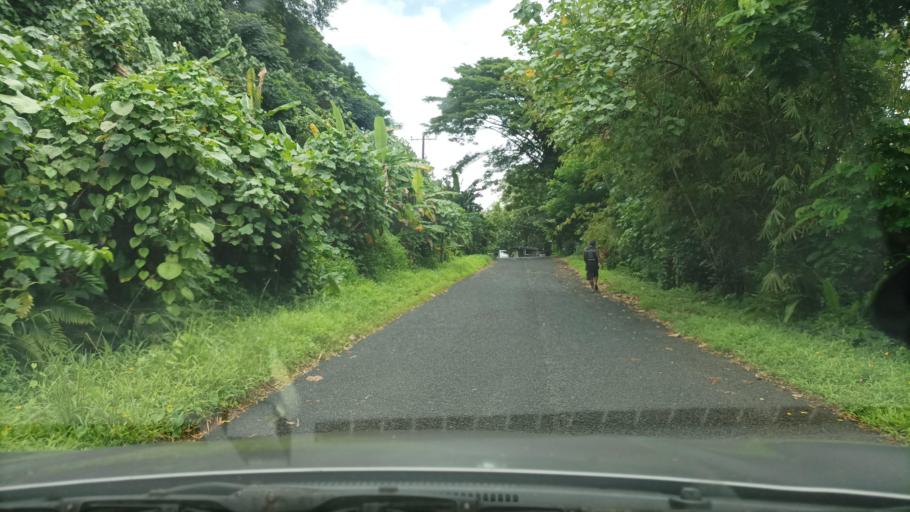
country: FM
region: Pohnpei
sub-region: Madolenihm Municipality
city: Madolenihm Municipality Government
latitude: 6.8528
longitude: 158.2970
